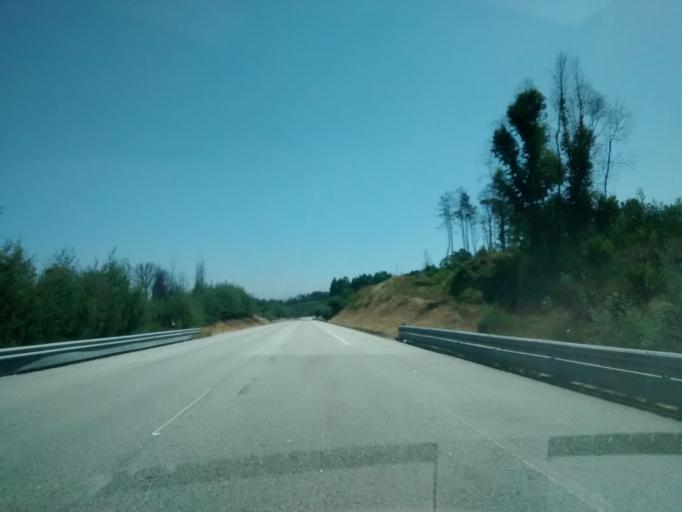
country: PT
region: Coimbra
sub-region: Tabua
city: Tabua
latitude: 40.3727
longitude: -8.0318
